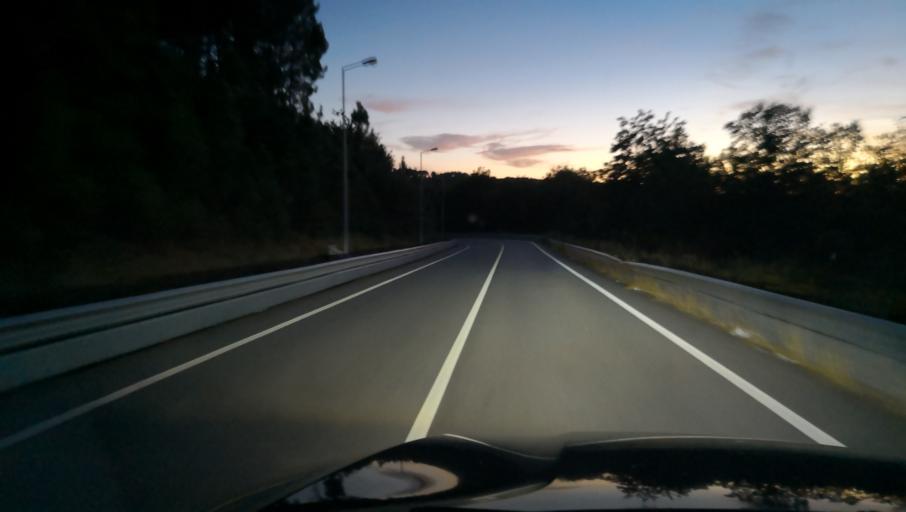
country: PT
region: Vila Real
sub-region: Sabrosa
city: Vilela
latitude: 41.2637
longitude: -7.6498
